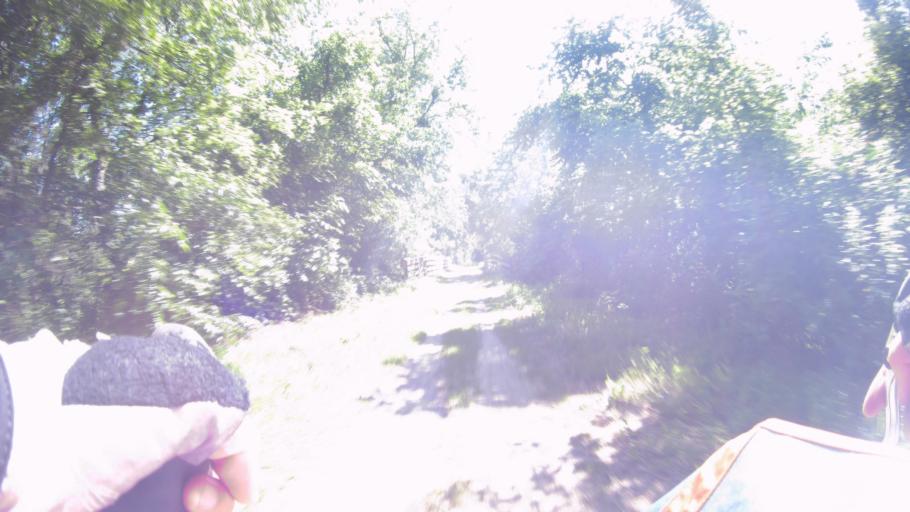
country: US
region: Wisconsin
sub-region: Dane County
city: Fitchburg
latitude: 42.9303
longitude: -89.5038
